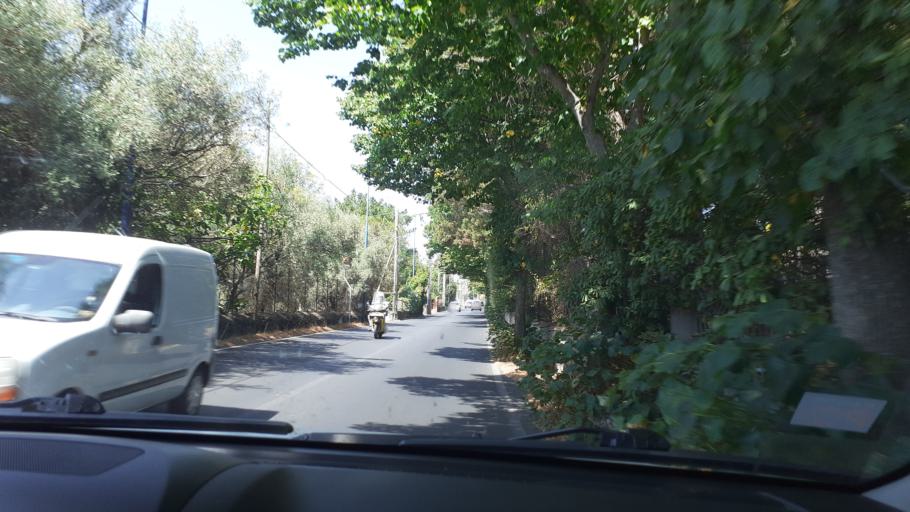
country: IT
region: Sicily
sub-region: Catania
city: Pedara
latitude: 37.6155
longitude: 15.0470
